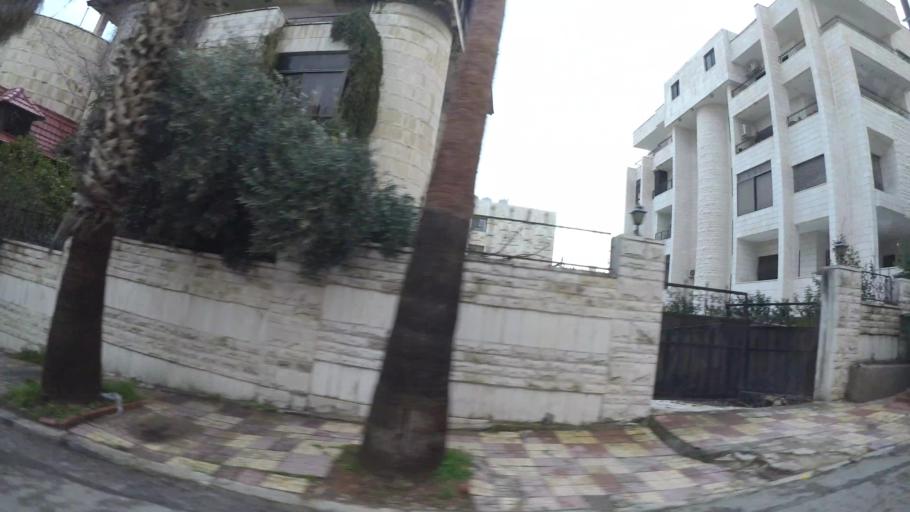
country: JO
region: Amman
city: Amman
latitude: 31.9634
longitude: 35.8848
